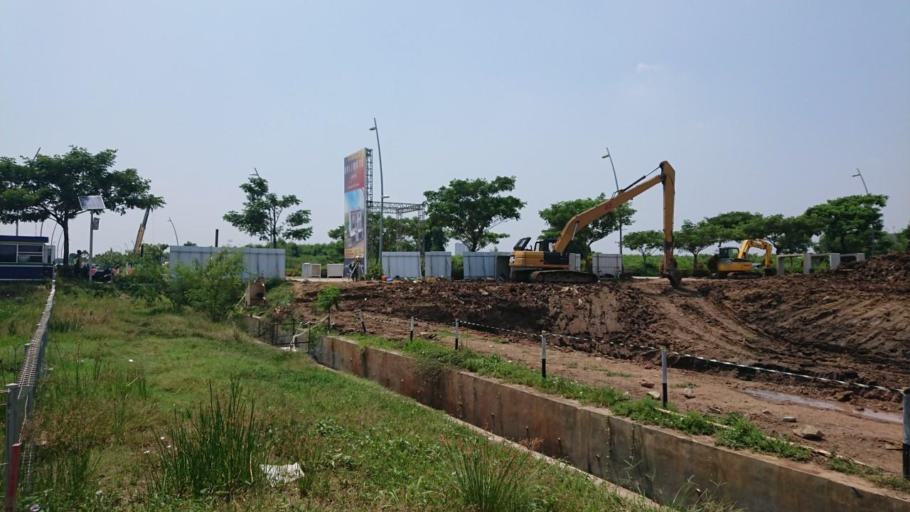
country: ID
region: West Java
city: Bekasi
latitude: -6.1622
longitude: 106.9579
